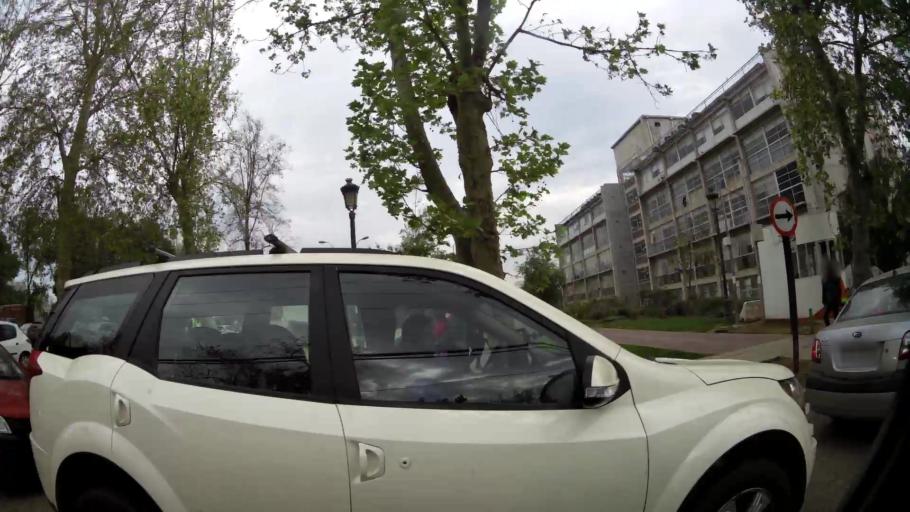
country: CL
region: Santiago Metropolitan
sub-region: Provincia de Santiago
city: Lo Prado
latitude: -33.5070
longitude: -70.7566
